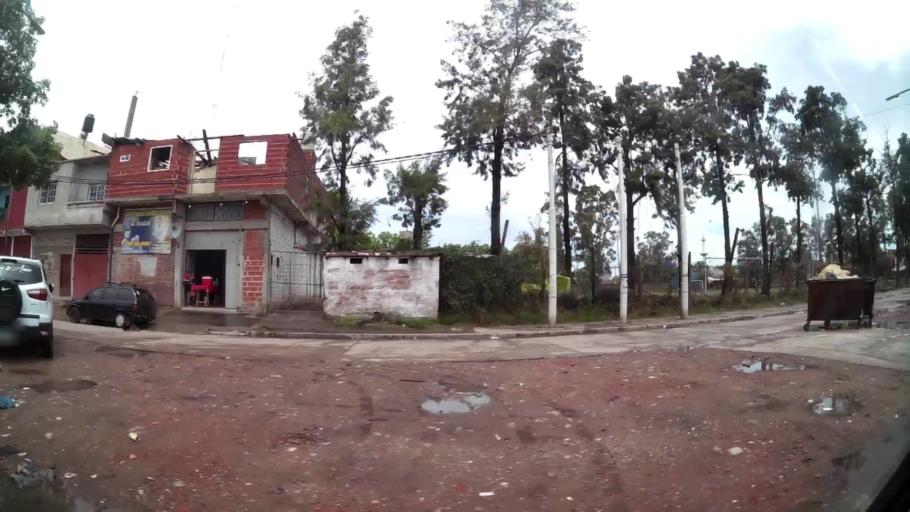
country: AR
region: Buenos Aires F.D.
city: Villa Lugano
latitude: -34.6569
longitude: -58.4512
